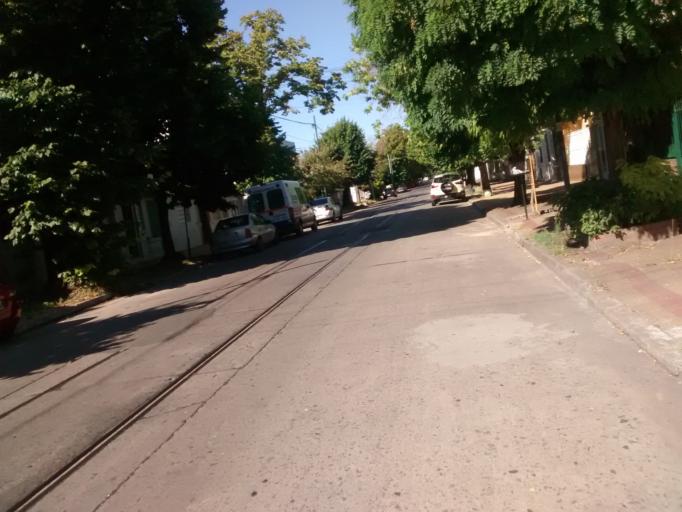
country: AR
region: Buenos Aires
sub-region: Partido de La Plata
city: La Plata
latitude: -34.9258
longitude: -57.9264
